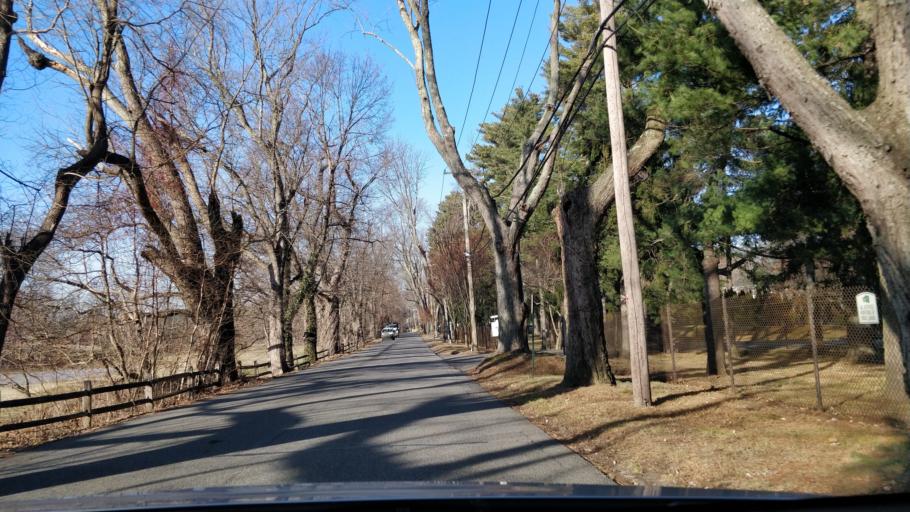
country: US
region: New York
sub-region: Nassau County
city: Old Brookville
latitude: 40.8174
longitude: -73.6075
